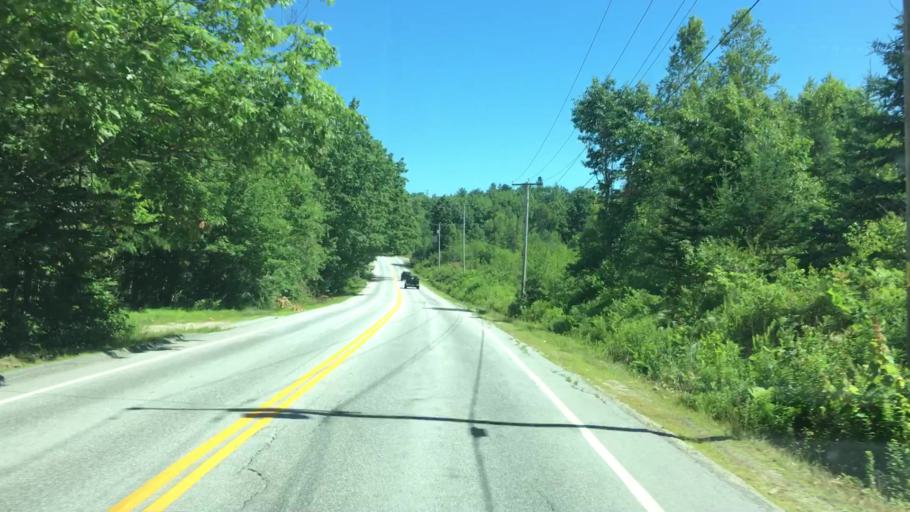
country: US
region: Maine
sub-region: Hancock County
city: Sedgwick
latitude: 44.3502
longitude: -68.6707
